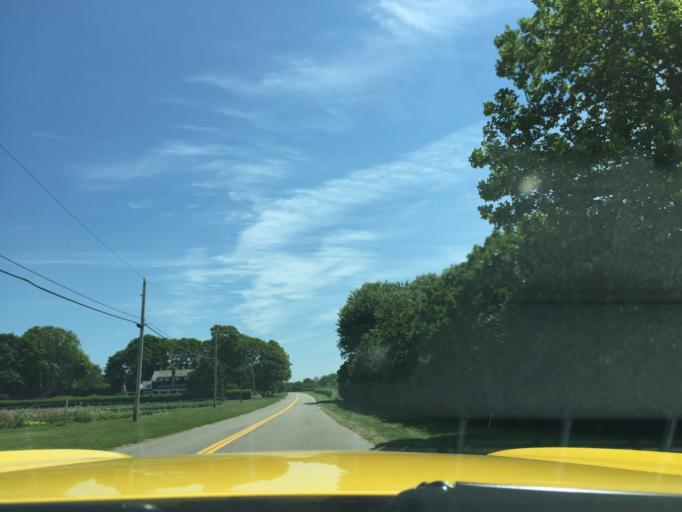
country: US
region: New York
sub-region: Suffolk County
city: Bridgehampton
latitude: 40.9317
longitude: -72.2746
